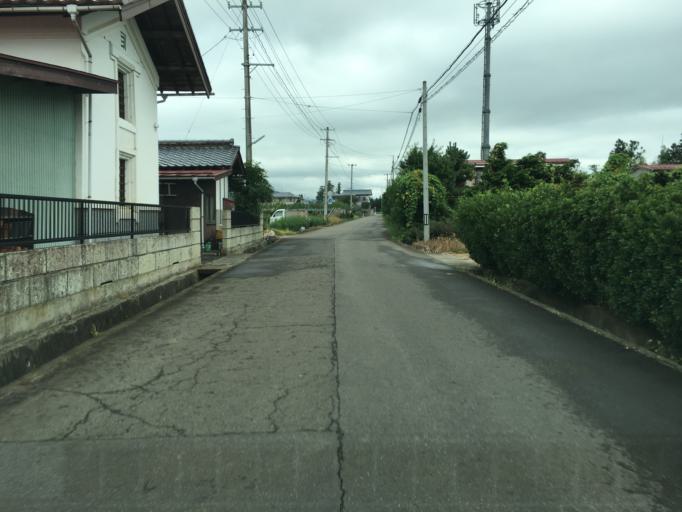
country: JP
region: Fukushima
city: Fukushima-shi
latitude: 37.7603
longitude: 140.4068
